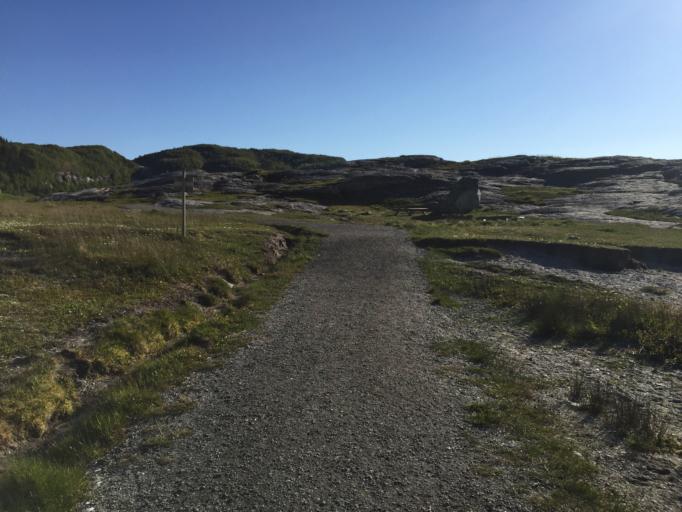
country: NO
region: Nordland
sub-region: Bodo
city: Loding
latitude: 67.4128
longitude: 14.6319
